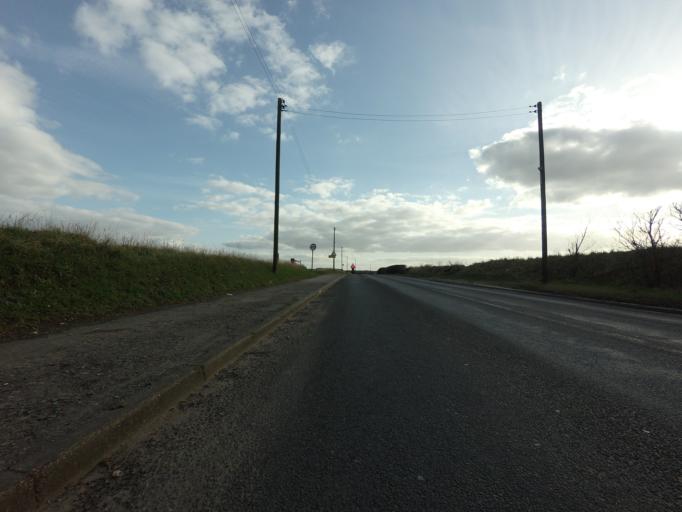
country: GB
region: England
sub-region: Kent
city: Dartford
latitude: 51.4190
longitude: 0.2017
